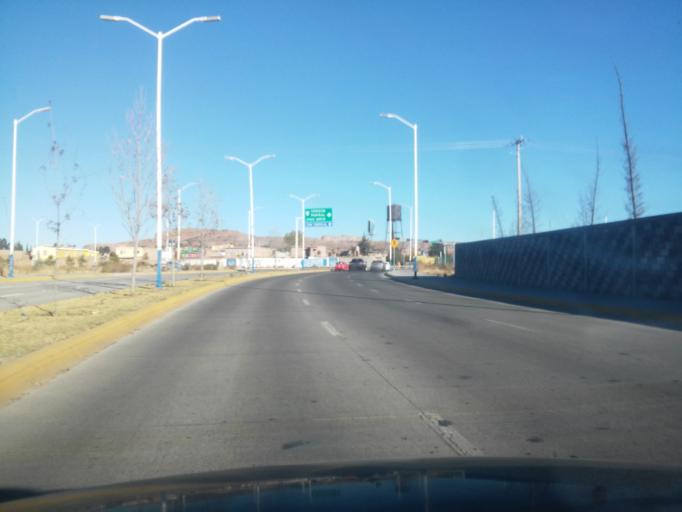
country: MX
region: Durango
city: Victoria de Durango
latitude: 24.0363
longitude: -104.6603
